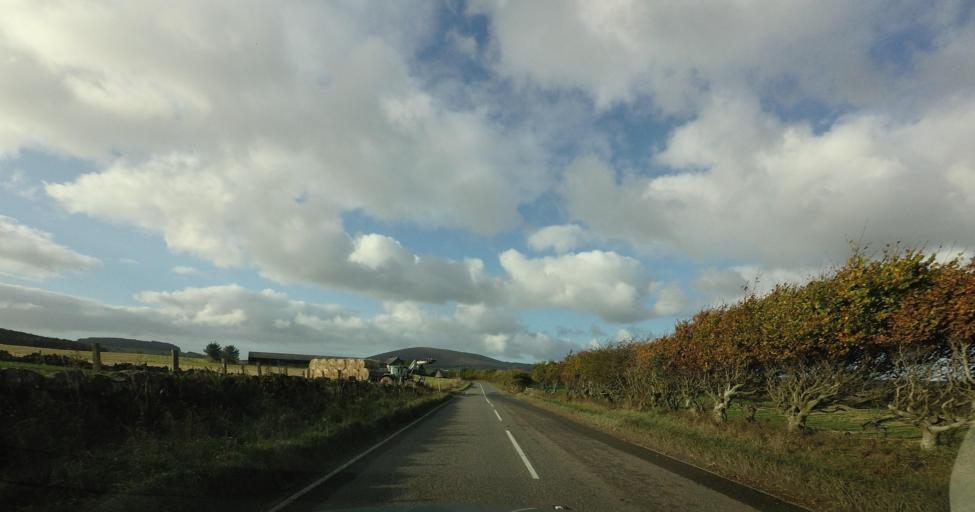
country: GB
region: Scotland
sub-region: Aberdeenshire
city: Portsoy
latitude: 57.6045
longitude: -2.7123
